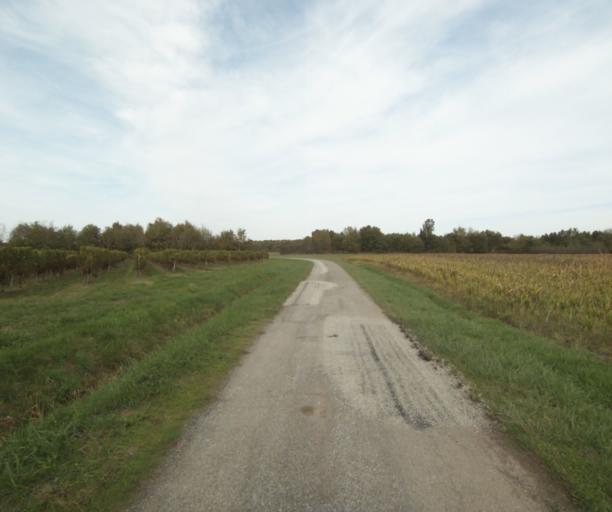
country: FR
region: Midi-Pyrenees
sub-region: Departement du Tarn-et-Garonne
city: Orgueil
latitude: 43.8771
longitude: 1.3883
